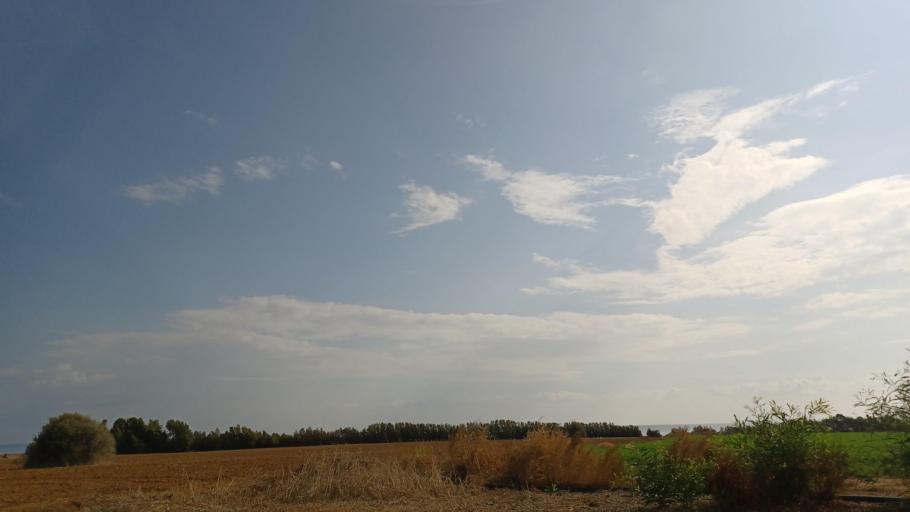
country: CY
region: Larnaka
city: Tersefanou
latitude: 34.8041
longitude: 33.5242
